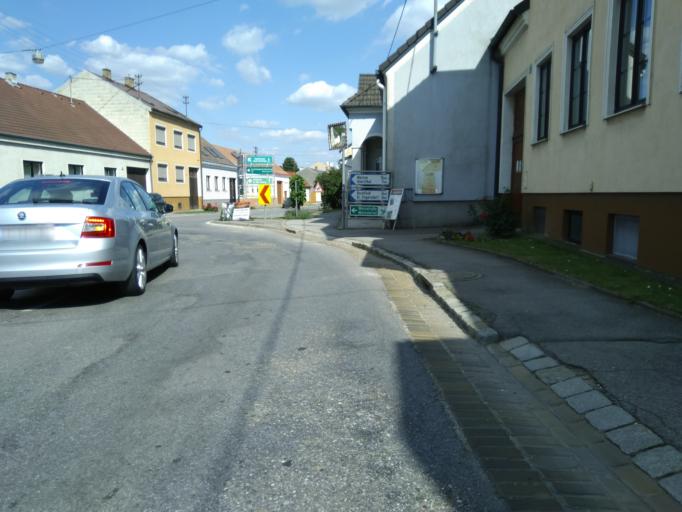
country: AT
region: Lower Austria
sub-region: Politischer Bezirk Mistelbach
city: Pillichsdorf
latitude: 48.3635
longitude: 16.5381
